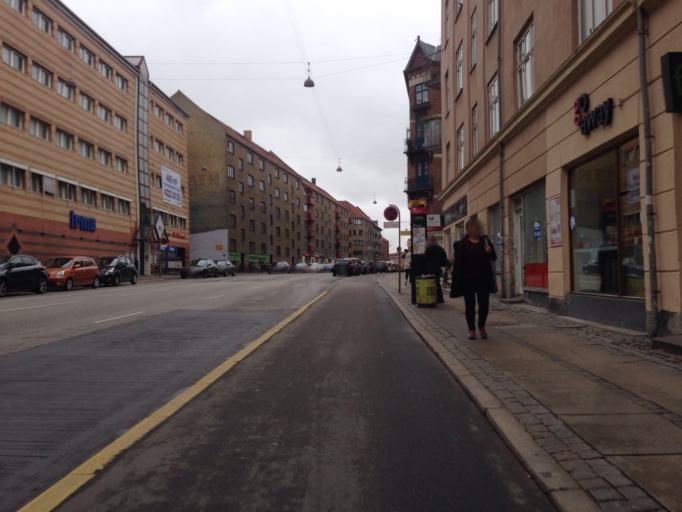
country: DK
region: Capital Region
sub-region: Frederiksberg Kommune
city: Frederiksberg
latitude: 55.7017
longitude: 12.5504
